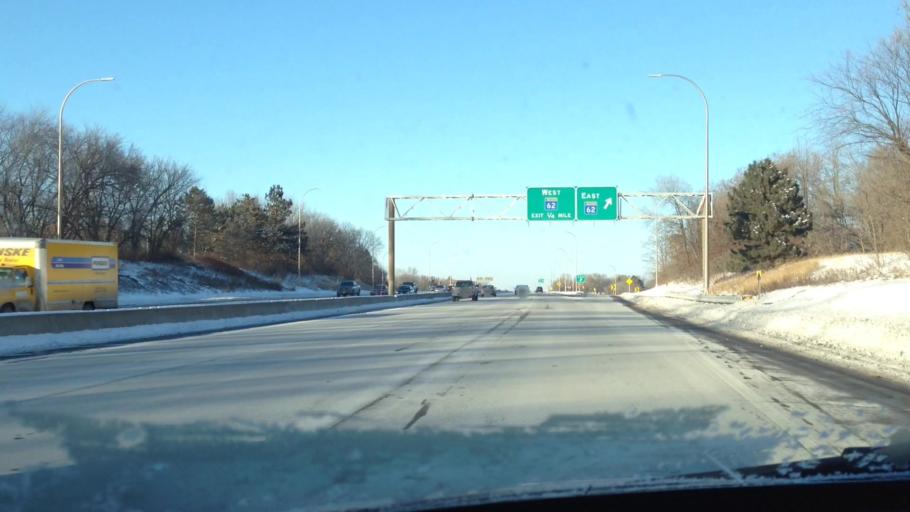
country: US
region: Minnesota
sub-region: Hennepin County
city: Edina
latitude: 44.8850
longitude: -93.3501
